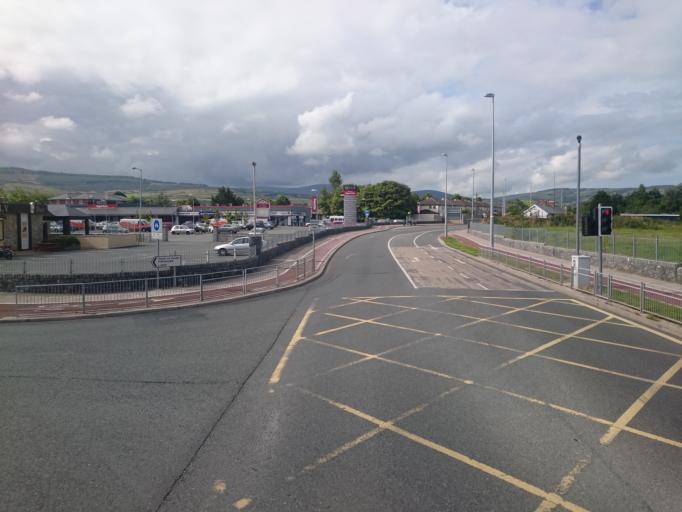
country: IE
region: Leinster
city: Firhouse
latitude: 53.2823
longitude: -6.3415
